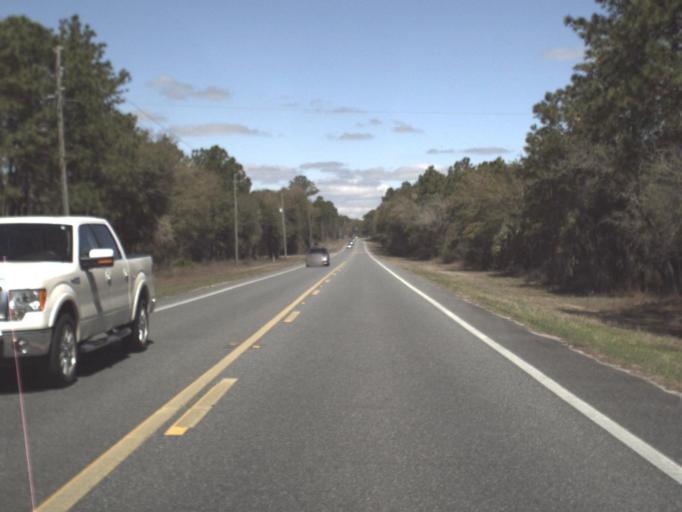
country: US
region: Florida
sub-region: Wakulla County
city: Crawfordville
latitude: 30.0694
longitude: -84.3890
